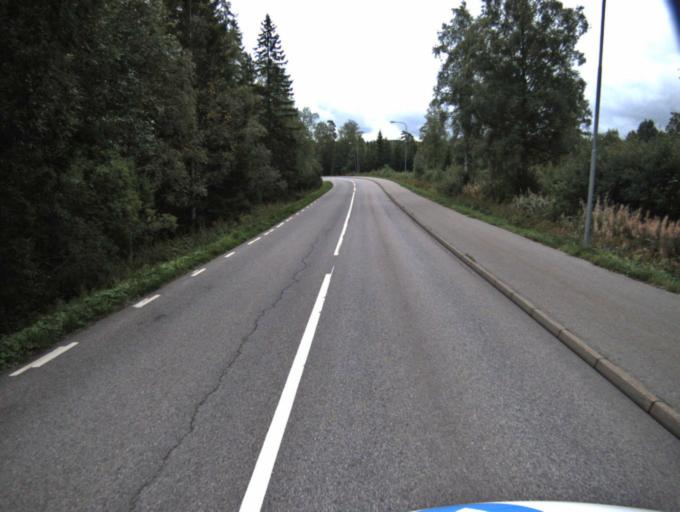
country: SE
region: Vaestra Goetaland
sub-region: Ulricehamns Kommun
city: Ulricehamn
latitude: 57.7703
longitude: 13.4450
